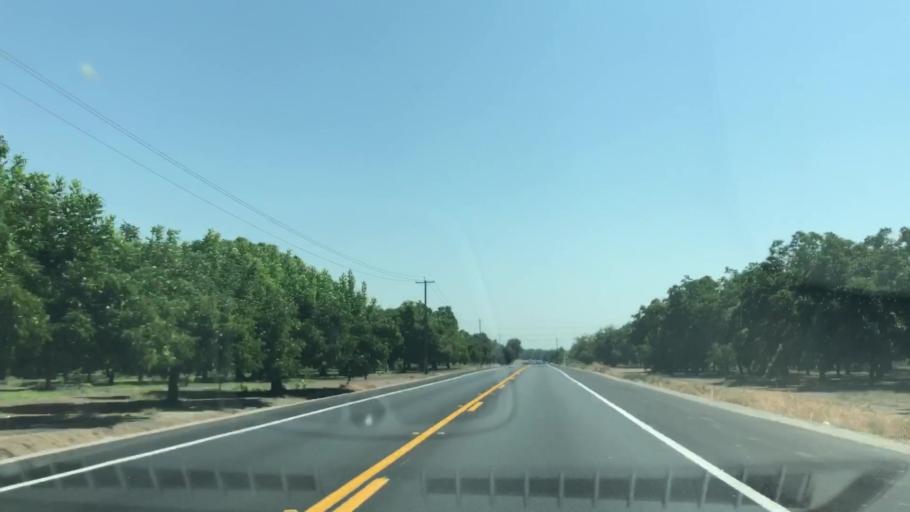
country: US
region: California
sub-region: San Joaquin County
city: Garden Acres
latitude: 37.9474
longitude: -121.1605
